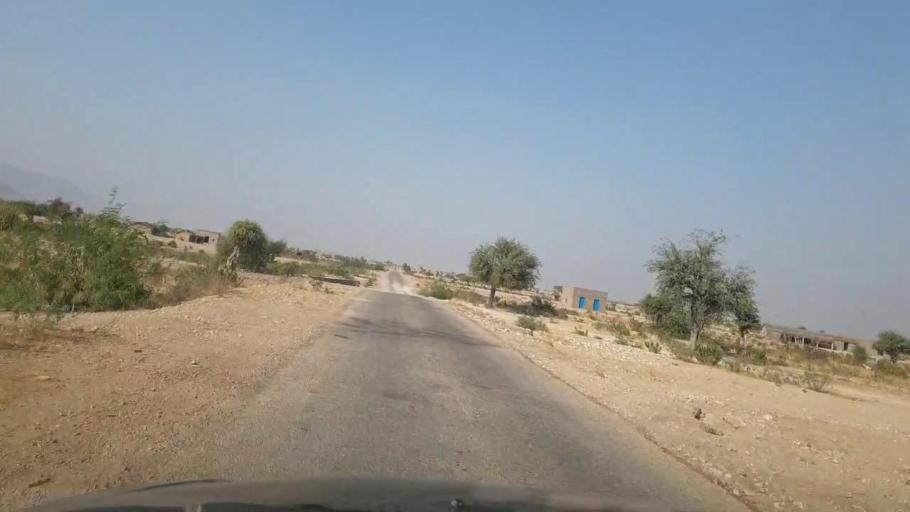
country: PK
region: Sindh
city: Jamshoro
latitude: 25.5936
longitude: 67.8179
